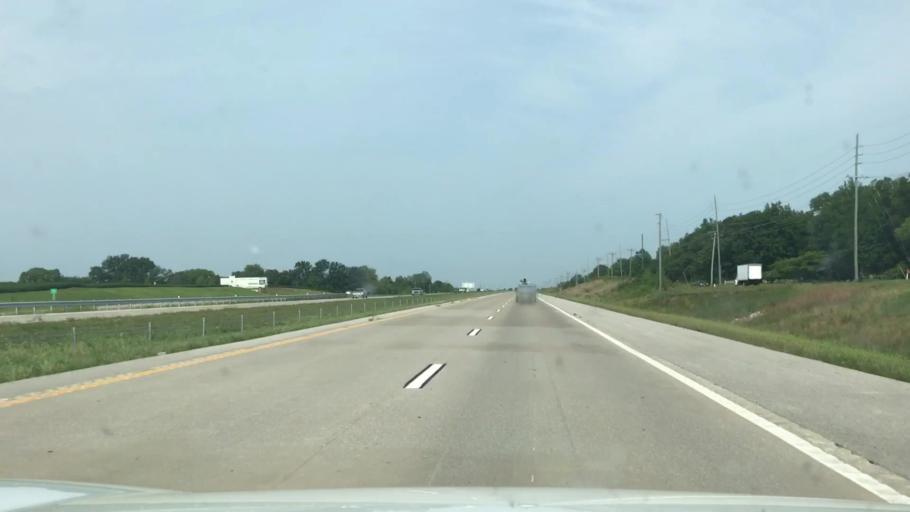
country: US
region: Missouri
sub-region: Saint Charles County
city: Dardenne Prairie
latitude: 38.7620
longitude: -90.7219
